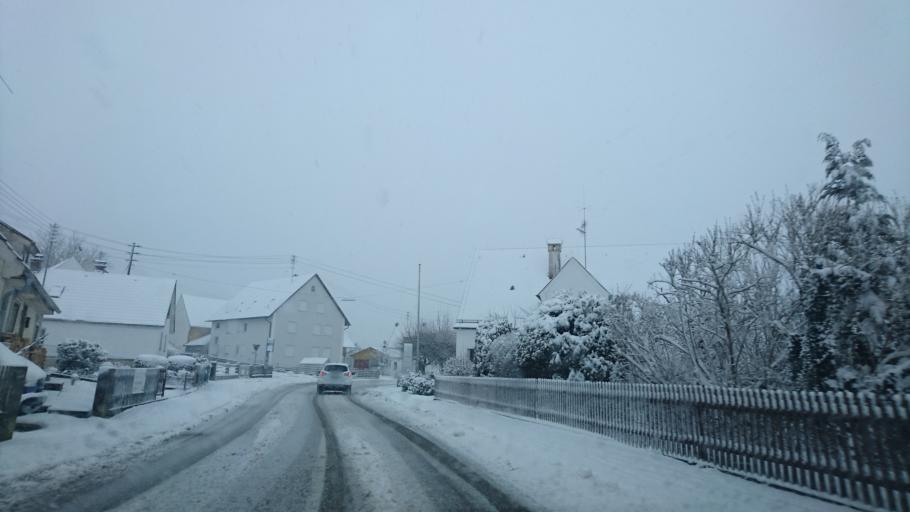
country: DE
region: Bavaria
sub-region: Swabia
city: Emersacker
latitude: 48.4910
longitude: 10.6721
